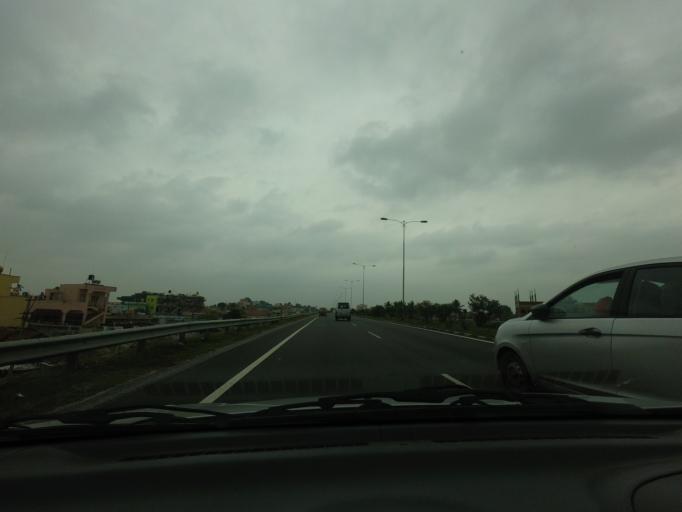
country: IN
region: Karnataka
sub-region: Mandya
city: Belluru
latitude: 12.9821
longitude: 76.8625
